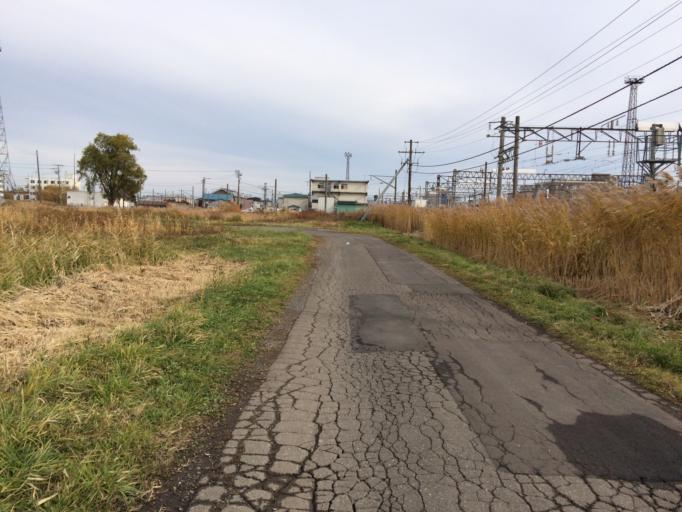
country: JP
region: Hokkaido
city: Iwamizawa
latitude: 43.2013
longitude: 141.7529
